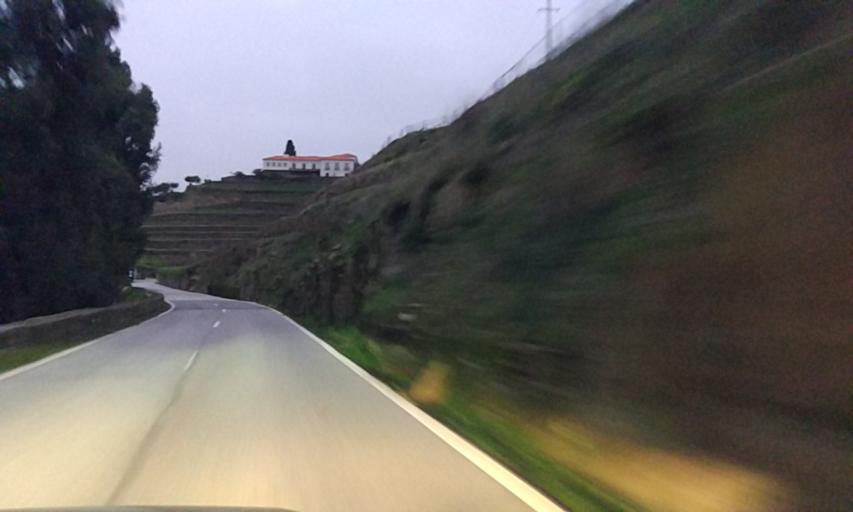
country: PT
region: Viseu
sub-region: Tabuaco
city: Tabuaco
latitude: 41.1607
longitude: -7.5758
